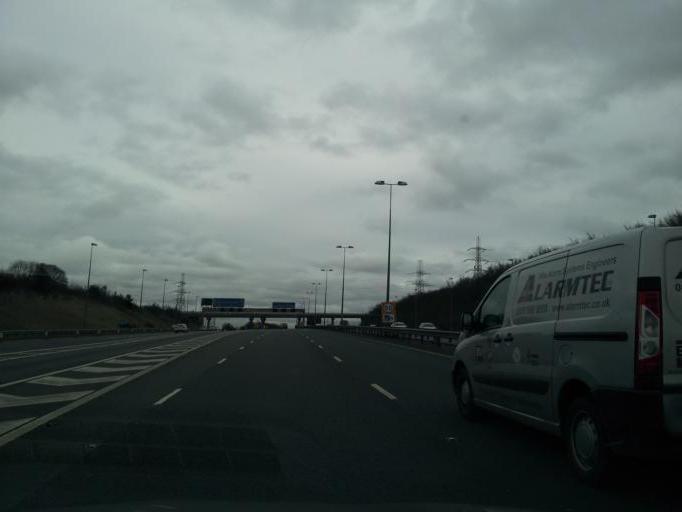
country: GB
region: England
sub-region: Staffordshire
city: Featherstone
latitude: 52.6722
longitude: -2.0785
